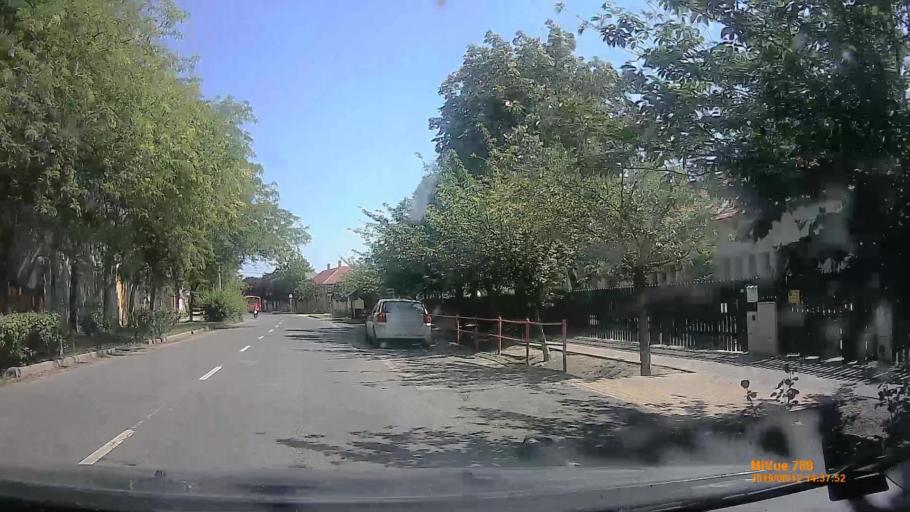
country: HU
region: Csongrad
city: Mako
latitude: 46.2113
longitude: 20.4743
